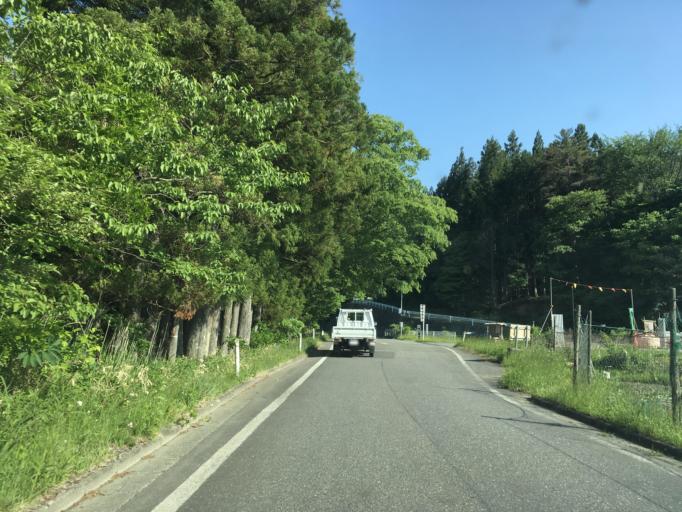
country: JP
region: Iwate
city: Kamaishi
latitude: 39.1945
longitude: 141.8412
